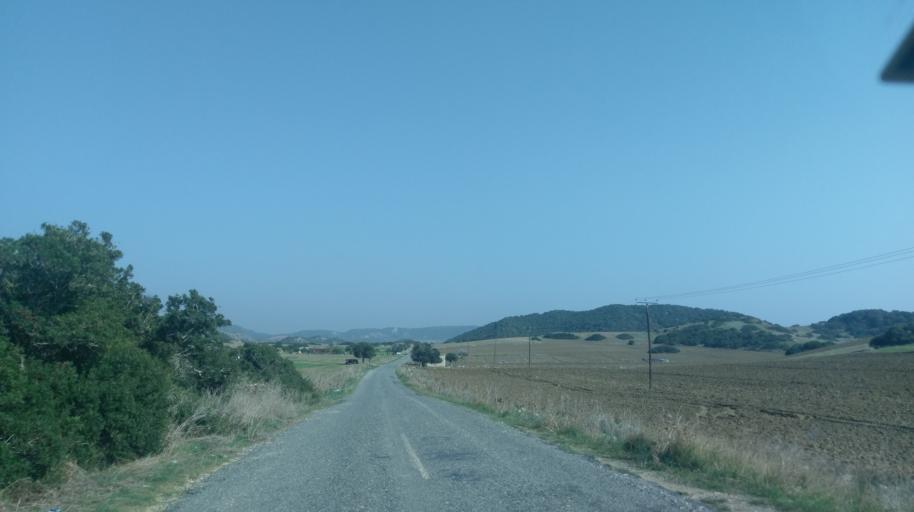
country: CY
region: Ammochostos
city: Rizokarpaso
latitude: 35.6342
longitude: 34.5047
